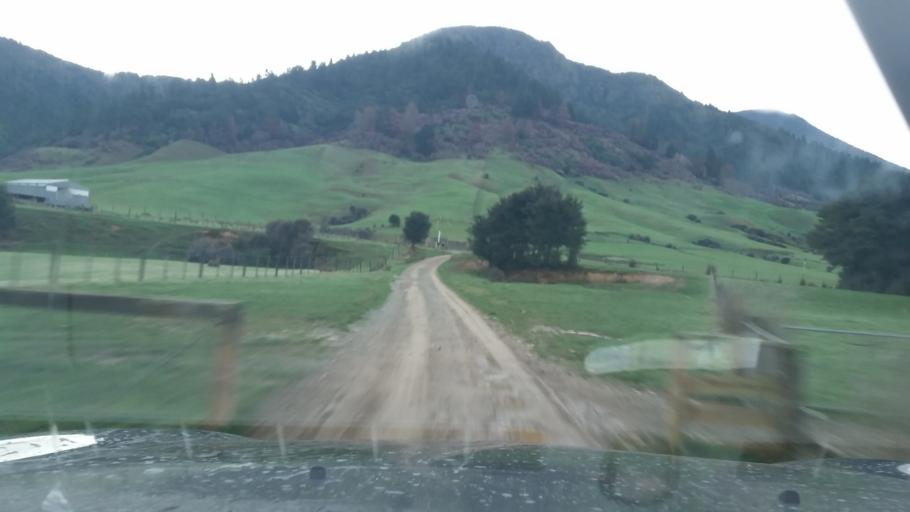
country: NZ
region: Marlborough
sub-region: Marlborough District
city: Picton
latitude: -41.1564
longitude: 174.1307
